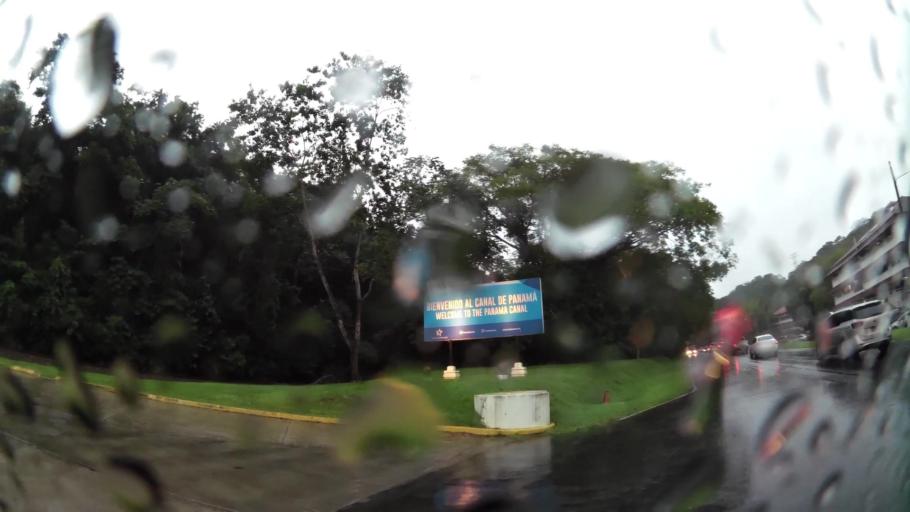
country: PA
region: Panama
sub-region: Distrito de Panama
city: Paraiso
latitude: 9.0038
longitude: -79.5895
